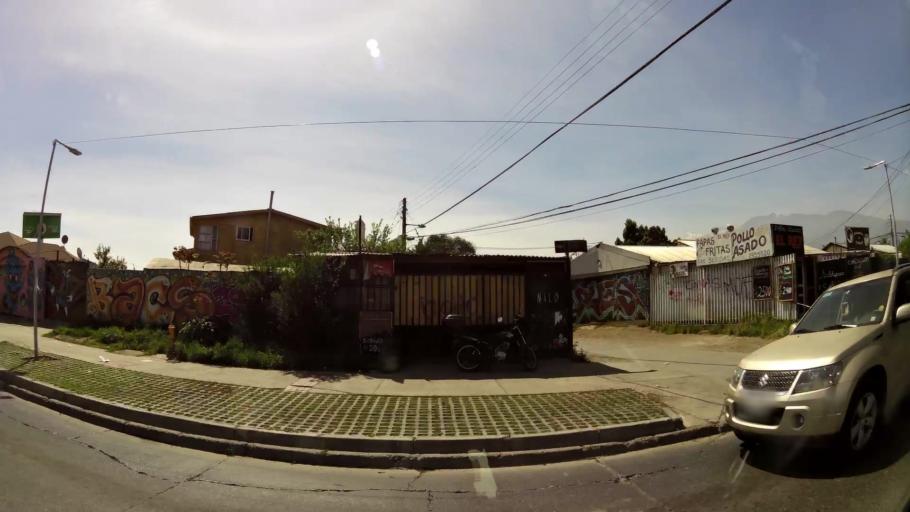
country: CL
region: Santiago Metropolitan
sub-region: Provincia de Cordillera
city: Puente Alto
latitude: -33.5762
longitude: -70.5779
